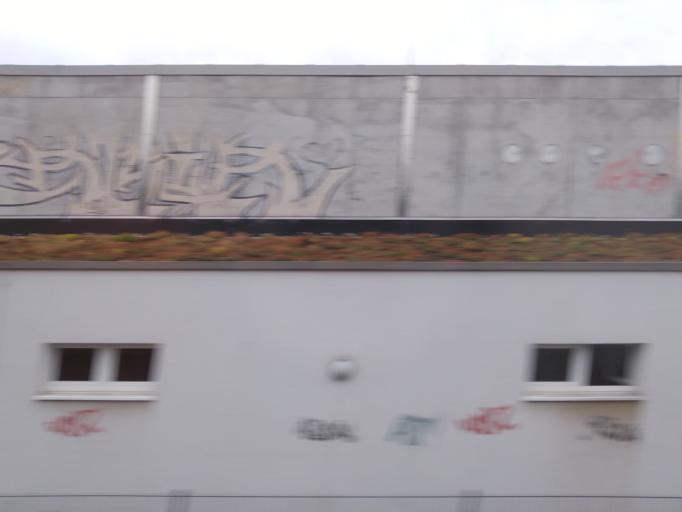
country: DE
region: Hesse
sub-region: Regierungsbezirk Darmstadt
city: Erzhausen
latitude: 49.9261
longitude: 8.6474
